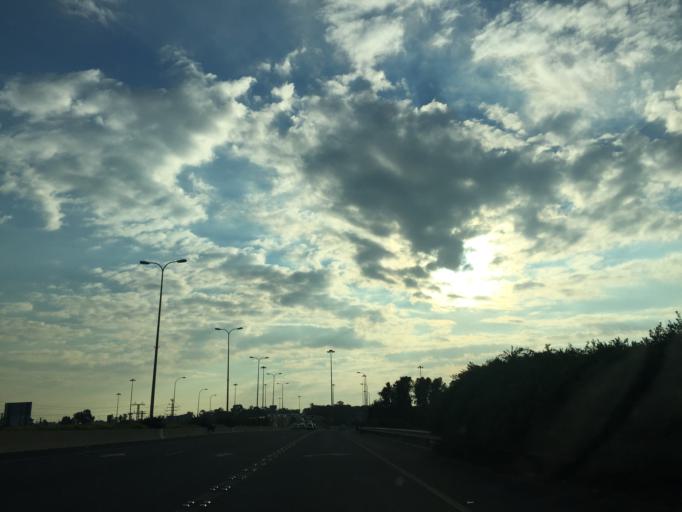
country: IL
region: Central District
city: Lod
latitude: 31.9274
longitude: 34.8872
